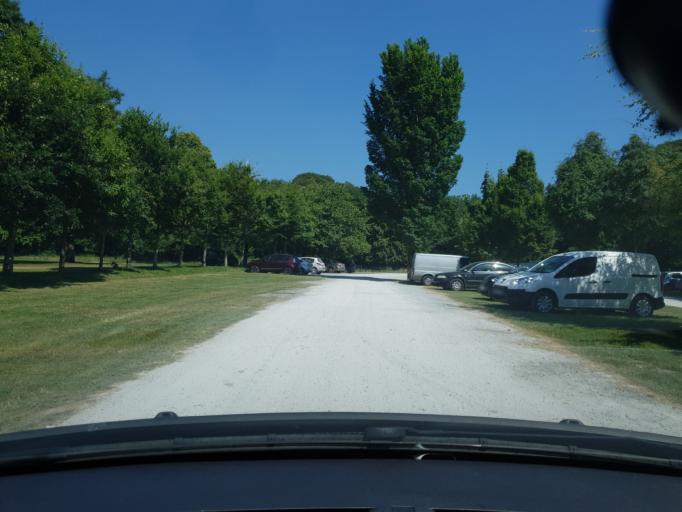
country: IE
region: Munster
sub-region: Ciarrai
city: Cill Airne
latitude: 52.0205
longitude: -9.5013
